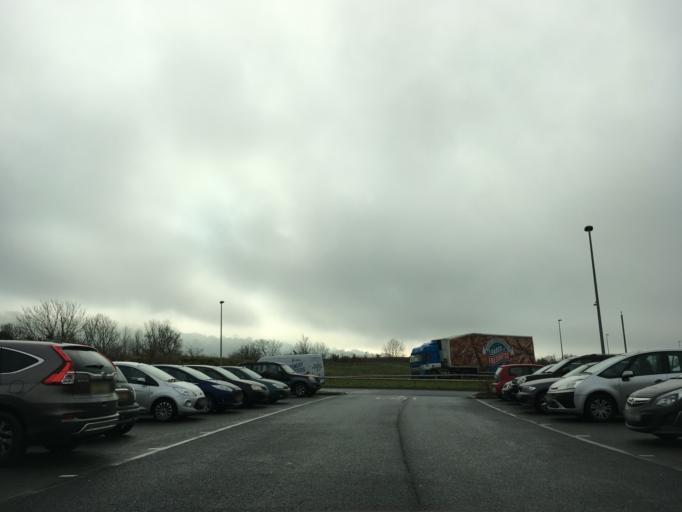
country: GB
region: England
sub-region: Gloucestershire
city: Painswick
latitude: 51.8204
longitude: -2.2267
